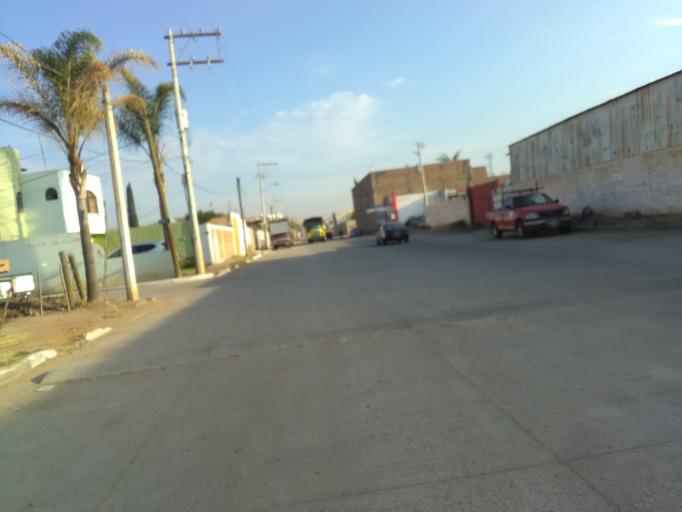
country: MX
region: Durango
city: Victoria de Durango
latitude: 24.0505
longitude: -104.6481
